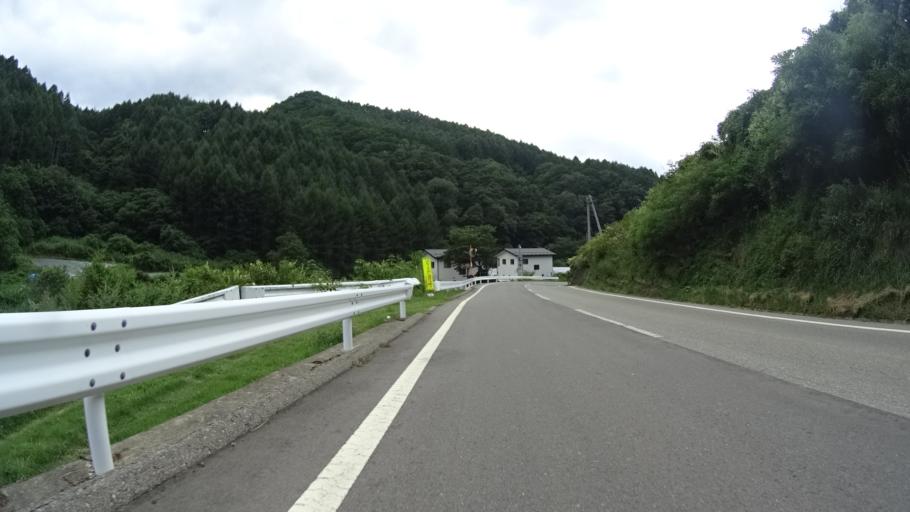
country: JP
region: Nagano
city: Saku
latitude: 36.0676
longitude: 138.5919
